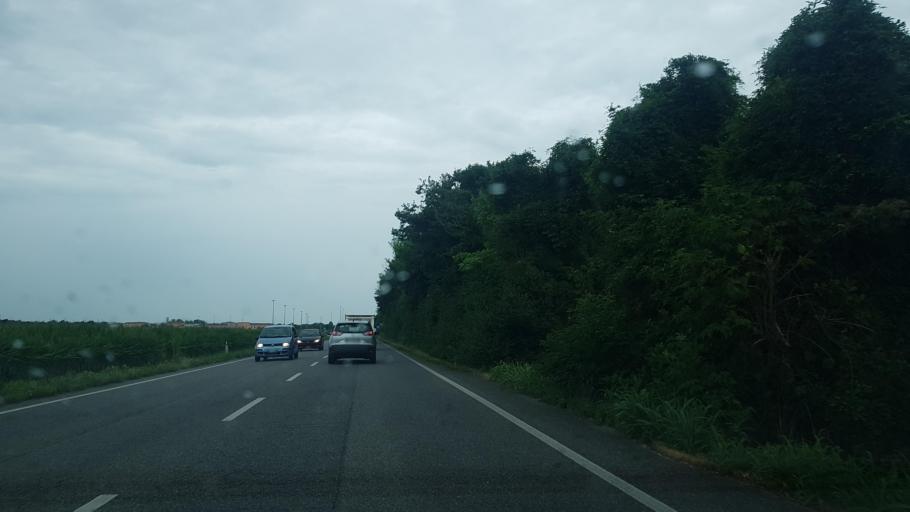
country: IT
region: Friuli Venezia Giulia
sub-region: Provincia di Udine
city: Visco
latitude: 45.8865
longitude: 13.3340
